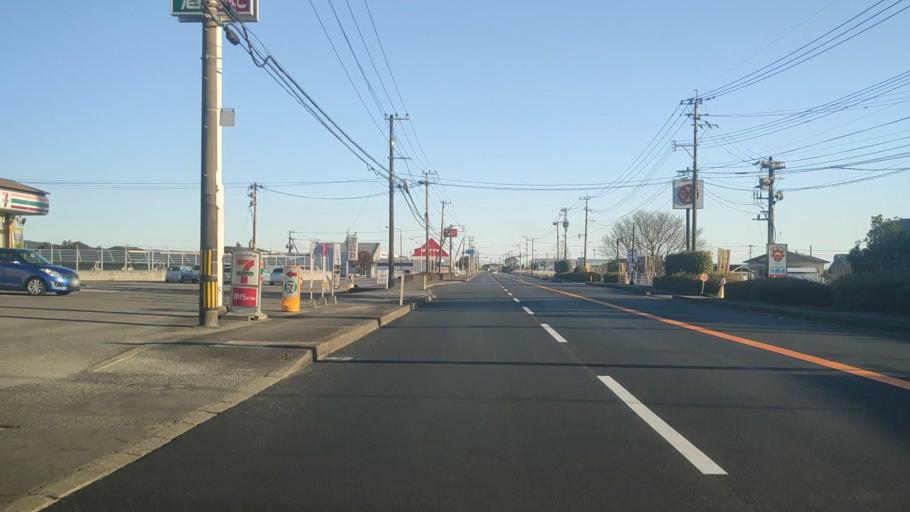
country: JP
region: Miyazaki
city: Takanabe
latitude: 32.2260
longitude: 131.5449
